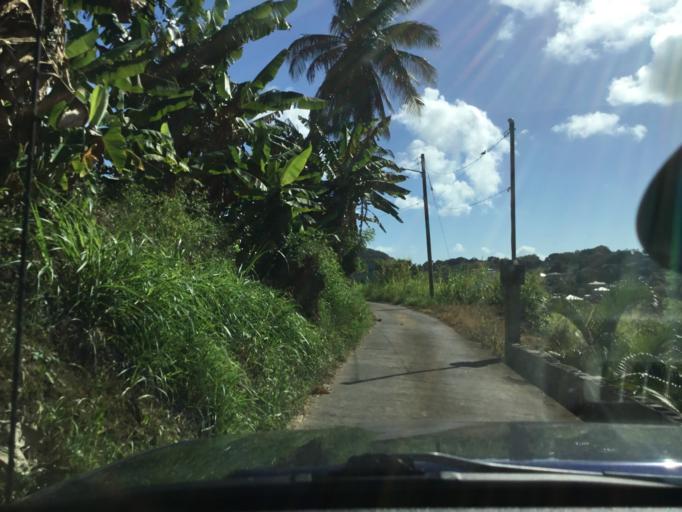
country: VC
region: Charlotte
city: Biabou
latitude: 13.1598
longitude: -61.1618
